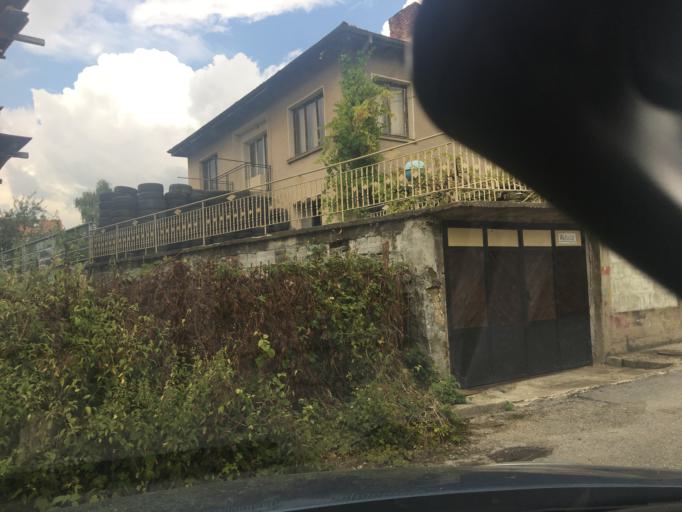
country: BG
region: Sofia-Capital
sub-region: Stolichna Obshtina
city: Sofia
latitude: 42.5857
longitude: 23.3680
